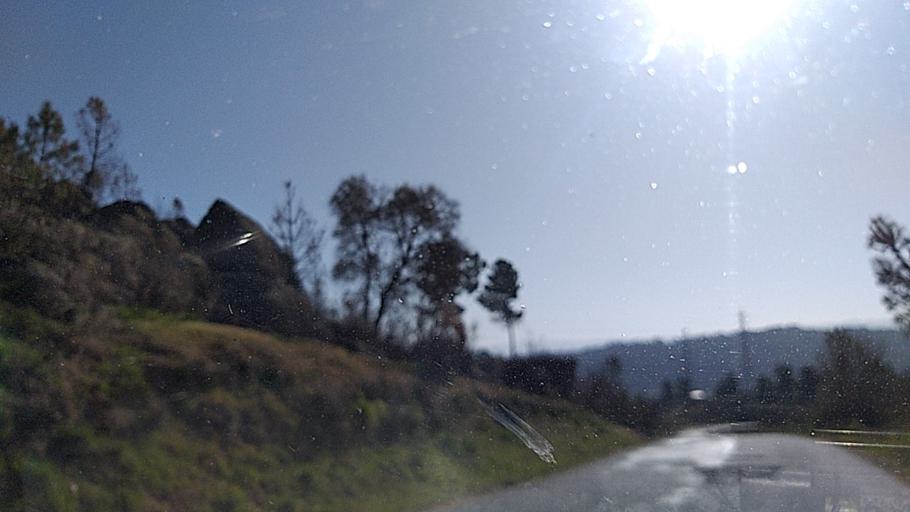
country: PT
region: Guarda
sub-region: Celorico da Beira
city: Celorico da Beira
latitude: 40.6884
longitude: -7.4179
